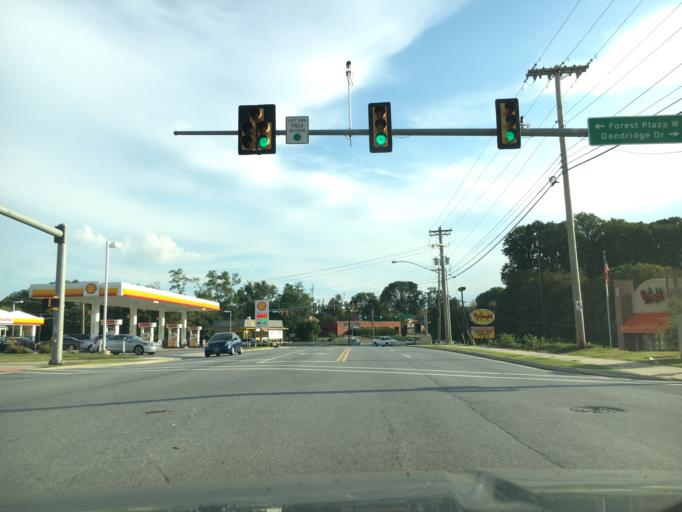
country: US
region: Virginia
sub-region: City of Lynchburg
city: West Lynchburg
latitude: 37.4120
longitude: -79.2123
